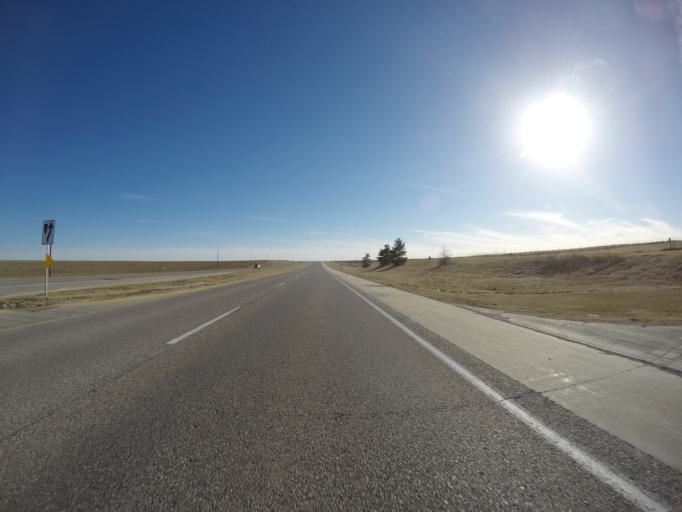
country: US
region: Nebraska
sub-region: Gage County
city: Beatrice
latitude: 40.4111
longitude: -96.7426
